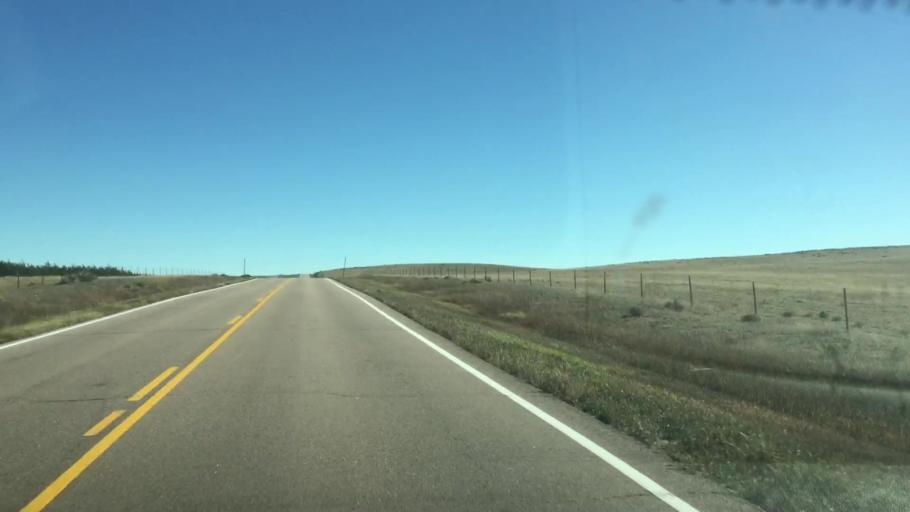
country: US
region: Colorado
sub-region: Lincoln County
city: Limon
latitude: 39.2828
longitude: -103.9871
